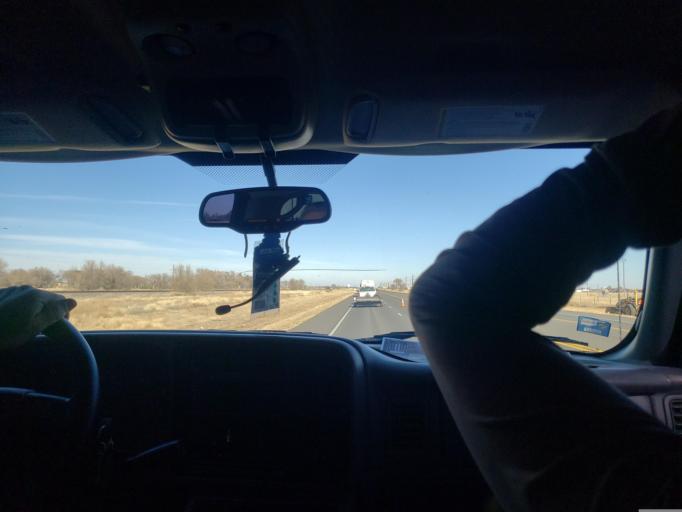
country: US
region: Texas
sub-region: Dallam County
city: Dalhart
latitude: 36.0376
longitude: -102.5618
